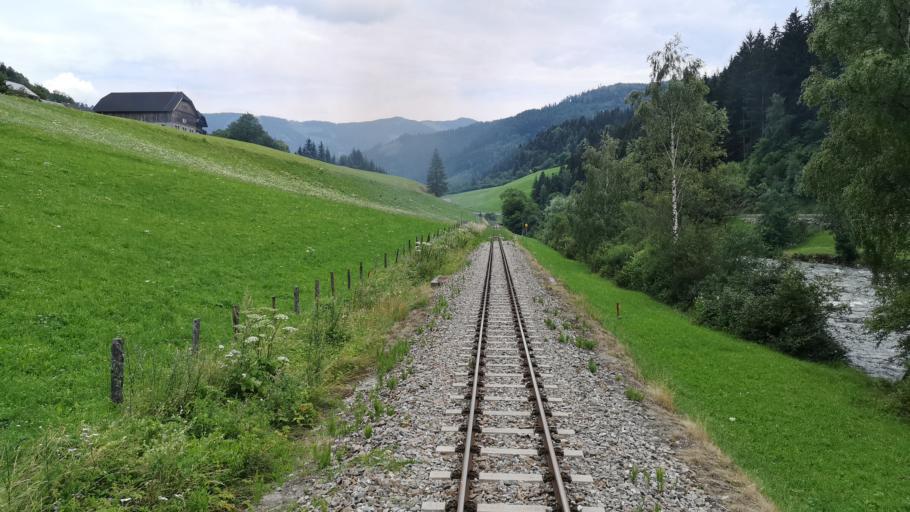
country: AT
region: Salzburg
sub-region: Politischer Bezirk Tamsweg
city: Ramingstein
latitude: 47.0731
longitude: 13.8640
